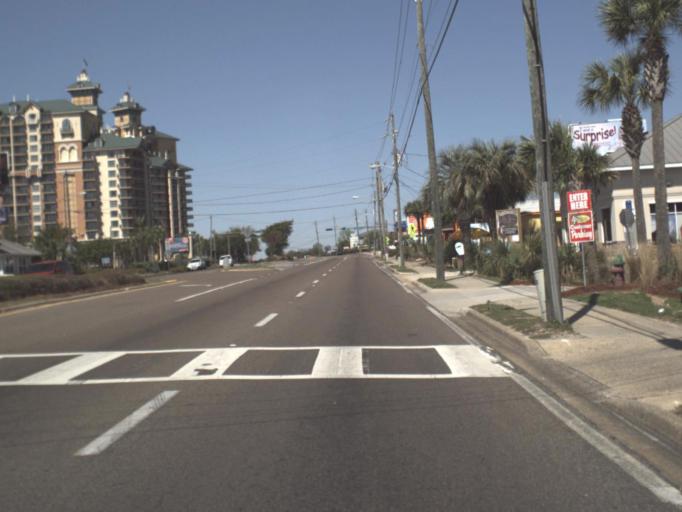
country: US
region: Florida
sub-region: Okaloosa County
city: Destin
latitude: 30.3950
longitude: -86.5084
